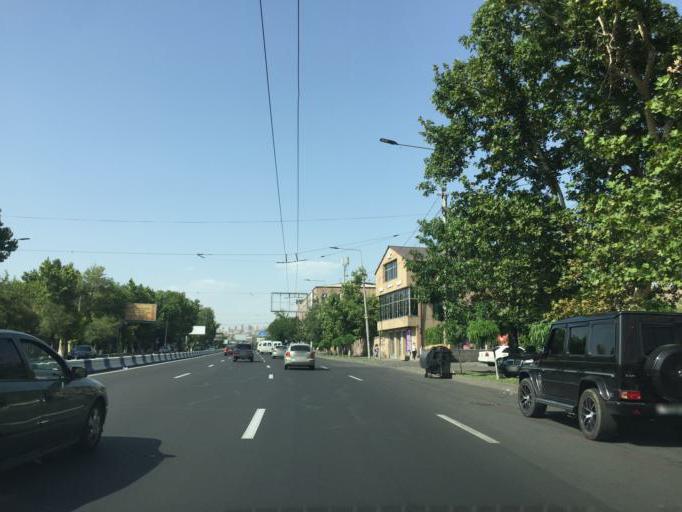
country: AM
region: Yerevan
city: Yerevan
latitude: 40.1587
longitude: 44.5028
